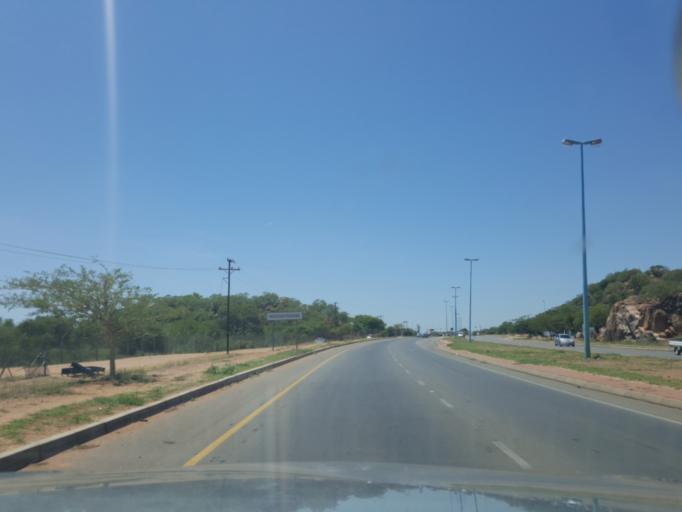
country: BW
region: Kweneng
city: Gaphatshwe
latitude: -24.5979
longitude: 25.8532
